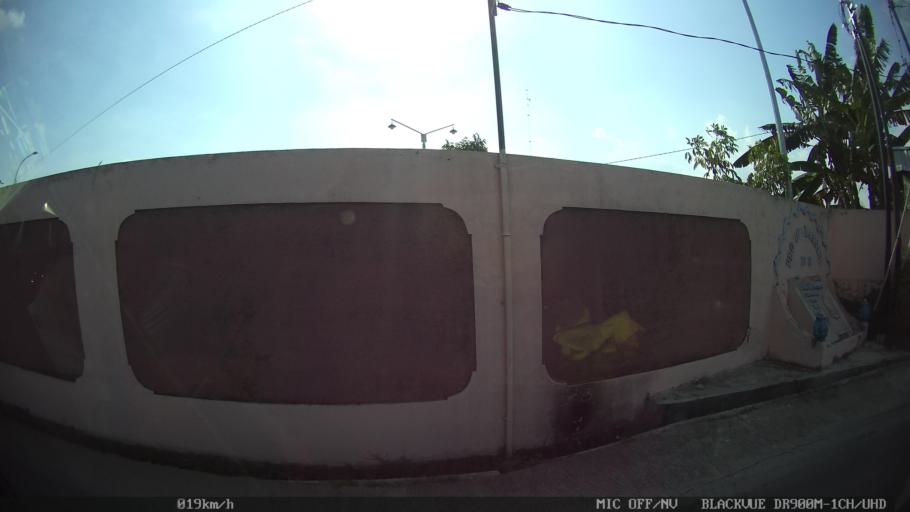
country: ID
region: Daerah Istimewa Yogyakarta
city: Sewon
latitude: -7.8345
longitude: 110.4011
